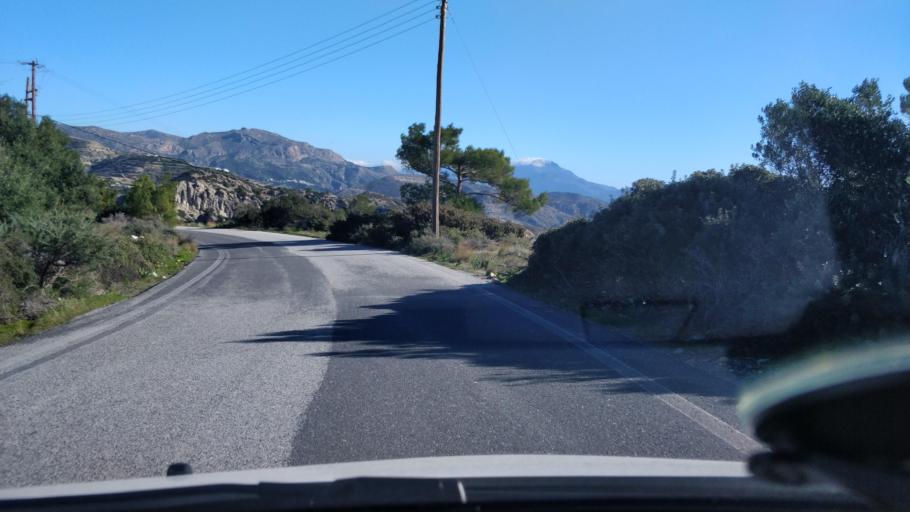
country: GR
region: Crete
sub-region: Nomos Lasithiou
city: Gra Liyia
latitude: 35.0369
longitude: 25.6678
